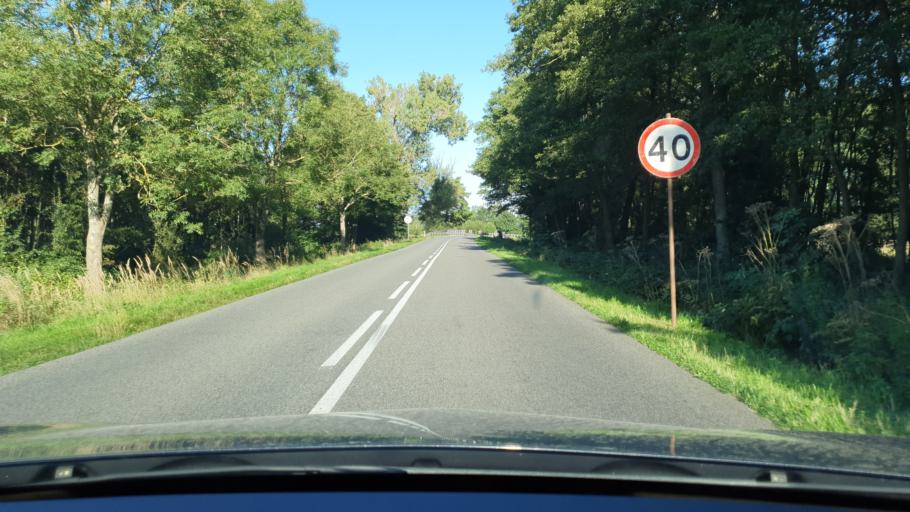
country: PL
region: West Pomeranian Voivodeship
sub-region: Powiat goleniowski
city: Przybiernow
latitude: 53.8249
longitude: 14.8603
